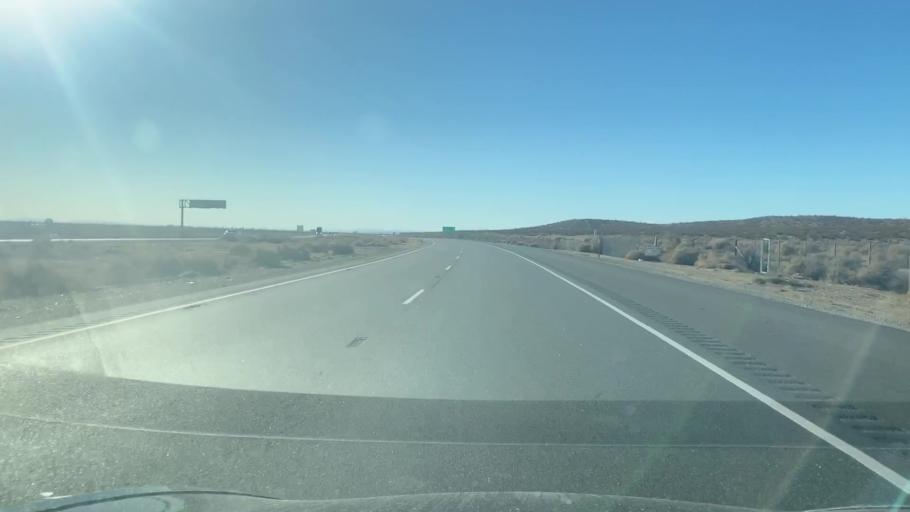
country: US
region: California
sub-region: Kern County
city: Boron
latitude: 35.0100
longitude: -117.6550
